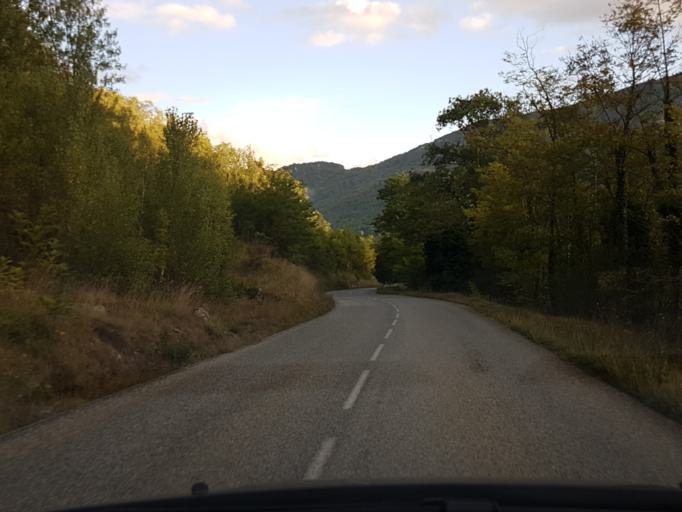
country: FR
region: Midi-Pyrenees
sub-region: Departement de l'Ariege
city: Tarascon-sur-Ariege
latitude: 42.8663
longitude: 1.5693
